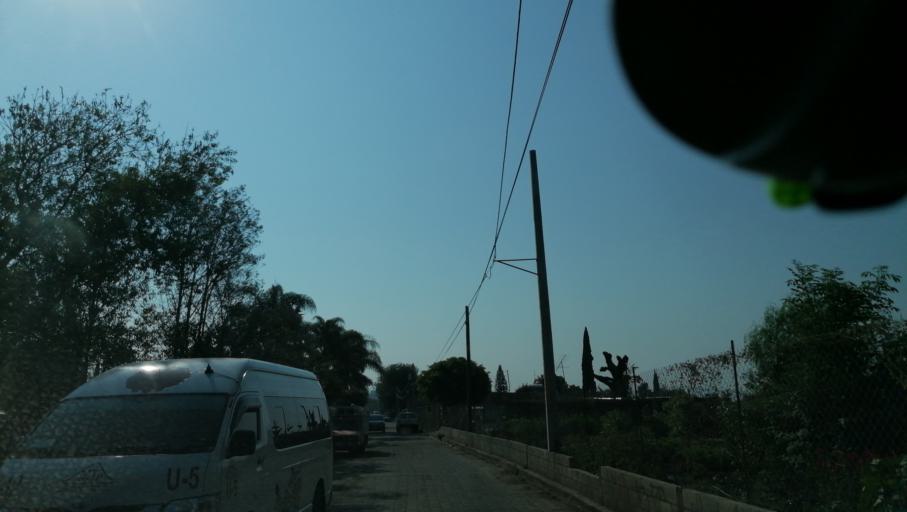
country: MX
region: Puebla
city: Atlixco
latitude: 18.9269
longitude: -98.4553
